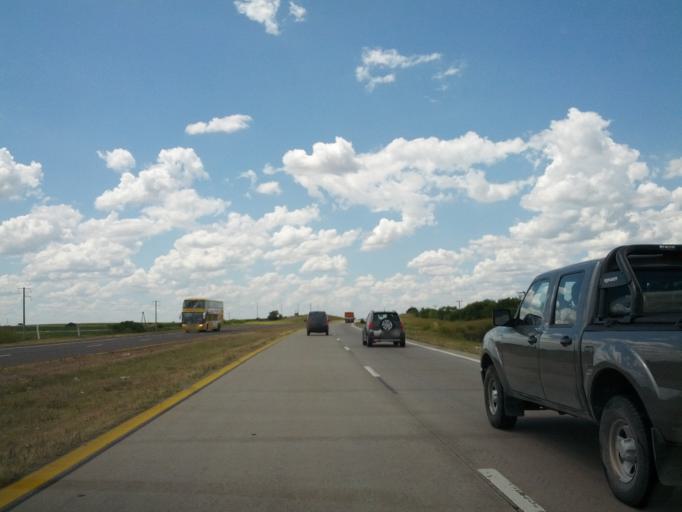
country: AR
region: Entre Rios
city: Gualeguaychu
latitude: -32.9177
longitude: -58.5652
